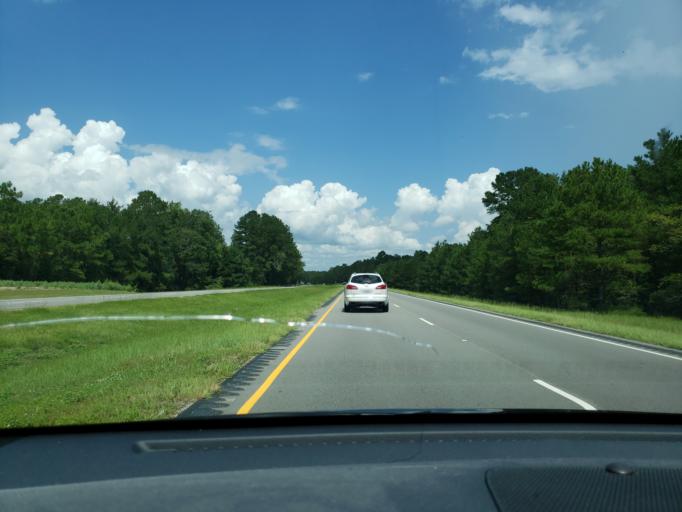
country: US
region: North Carolina
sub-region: Robeson County
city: Saint Pauls
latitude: 34.8498
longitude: -78.8523
